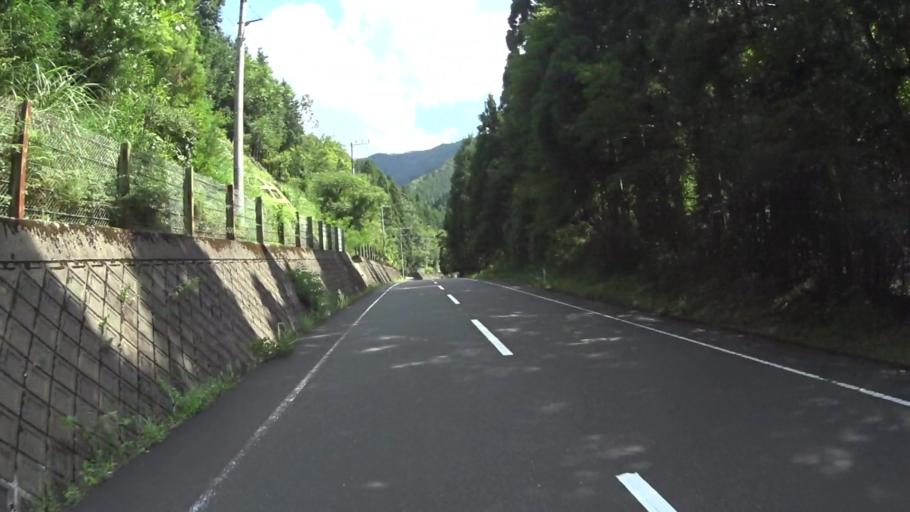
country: JP
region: Fukui
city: Obama
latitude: 35.2714
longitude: 135.5937
